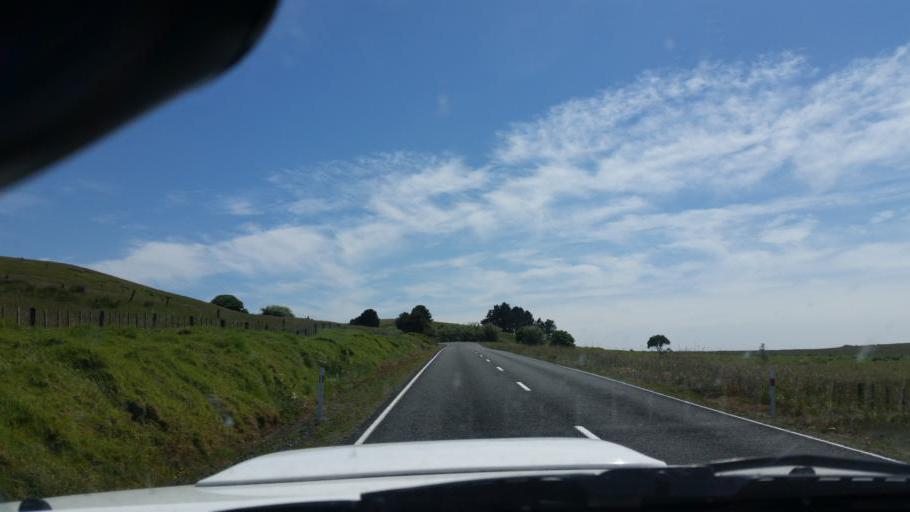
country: NZ
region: Auckland
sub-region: Auckland
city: Wellsford
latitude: -36.1865
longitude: 174.4103
